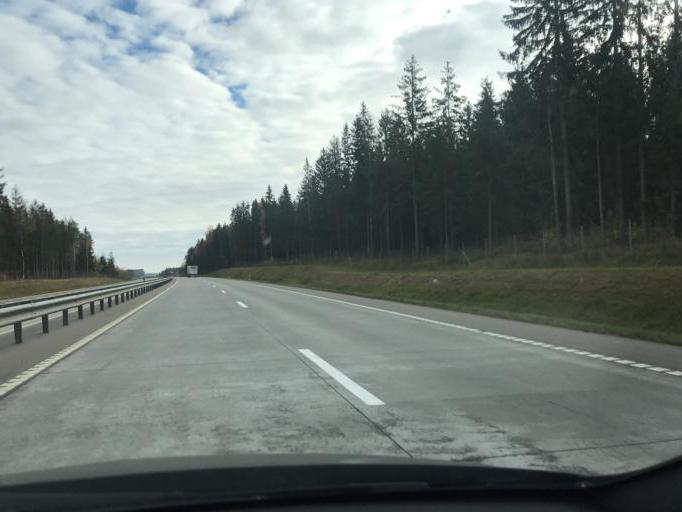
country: BY
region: Minsk
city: Zaslawye
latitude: 54.0663
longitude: 27.2998
